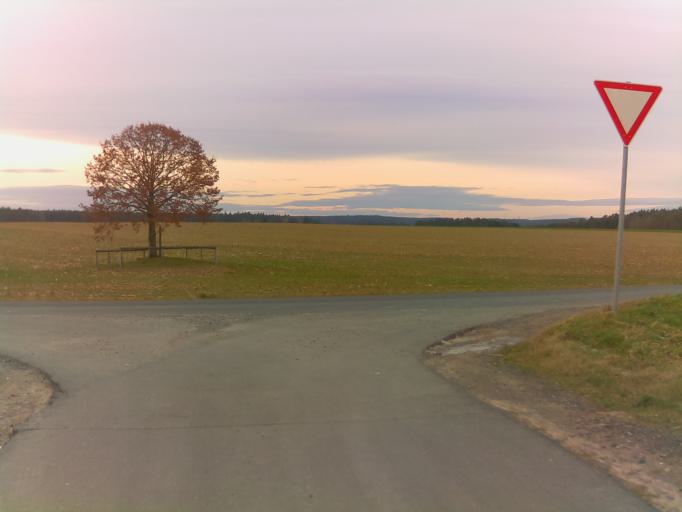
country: DE
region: Thuringia
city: Saara
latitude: 50.8630
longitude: 11.9545
